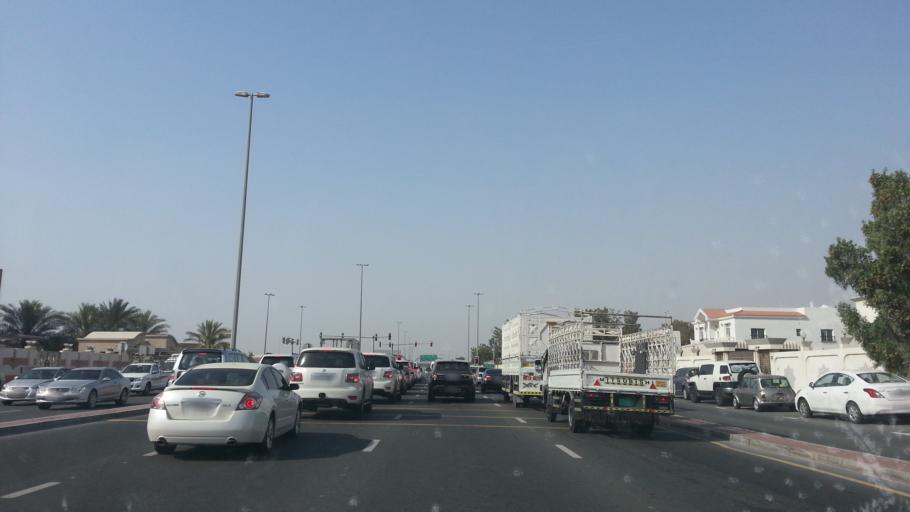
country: AE
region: Dubai
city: Dubai
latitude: 25.1112
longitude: 55.2073
